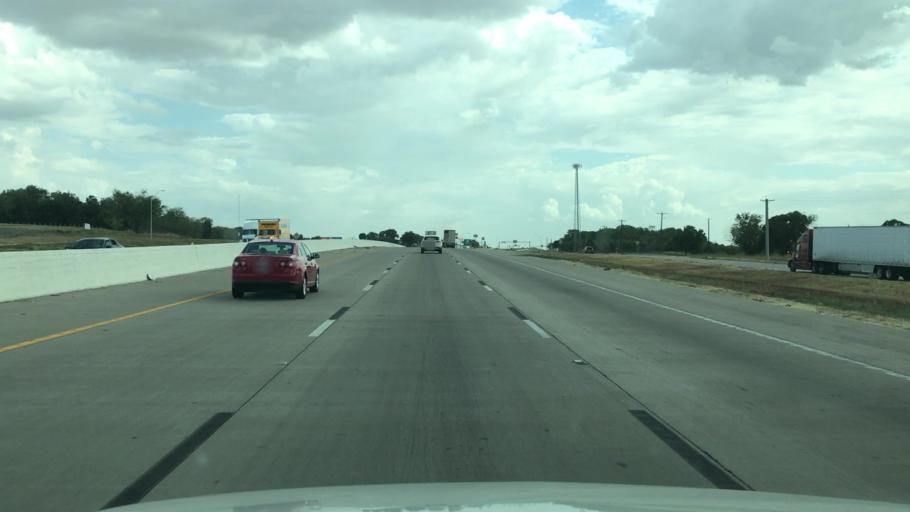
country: US
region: Texas
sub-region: McLennan County
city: West
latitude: 31.8143
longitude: -97.0985
